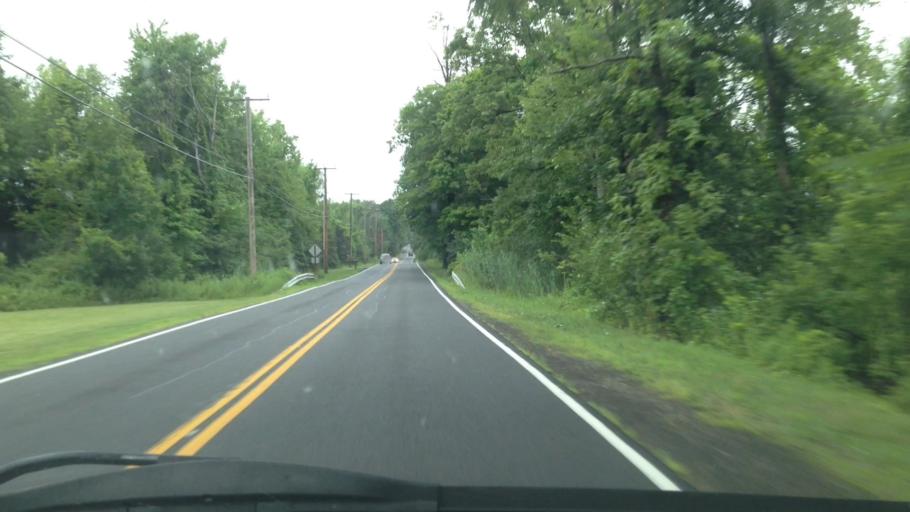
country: US
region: New York
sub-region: Ulster County
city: New Paltz
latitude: 41.7464
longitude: -74.0643
